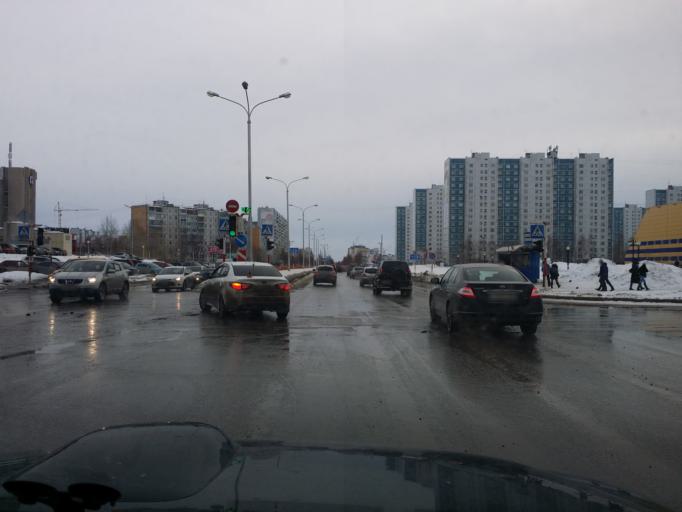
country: RU
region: Khanty-Mansiyskiy Avtonomnyy Okrug
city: Nizhnevartovsk
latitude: 60.9408
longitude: 76.5969
